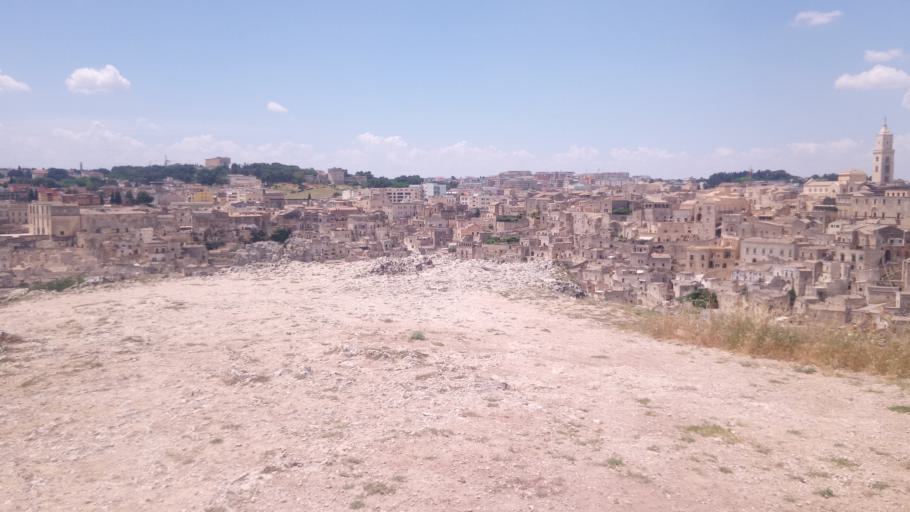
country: IT
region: Basilicate
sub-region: Provincia di Matera
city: Matera
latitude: 40.6644
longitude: 16.6164
